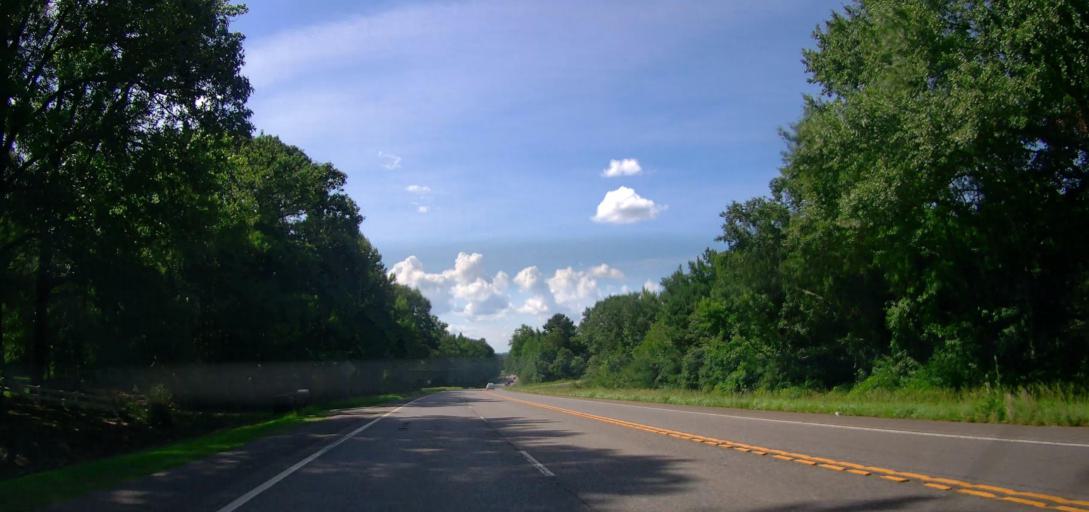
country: US
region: Alabama
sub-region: Pickens County
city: Gordo
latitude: 33.2907
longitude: -87.8705
